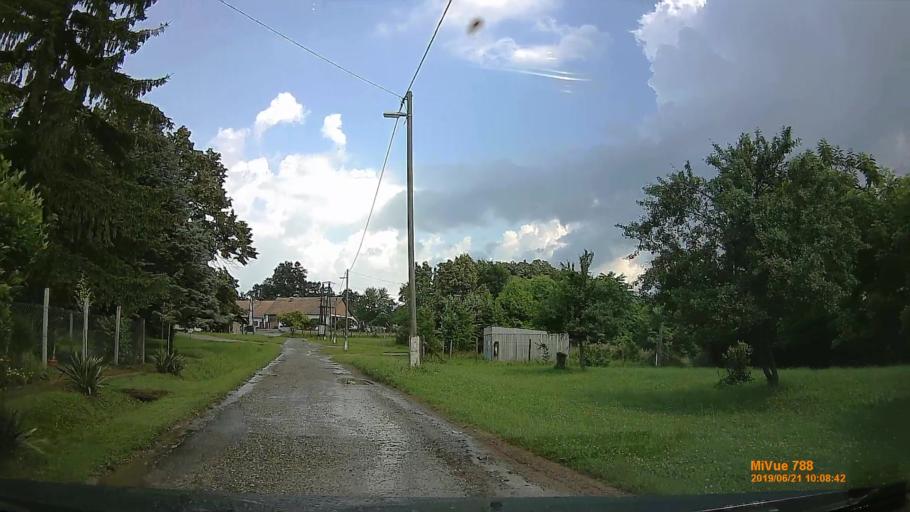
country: HU
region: Baranya
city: Buekkoesd
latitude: 46.1936
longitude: 17.9574
